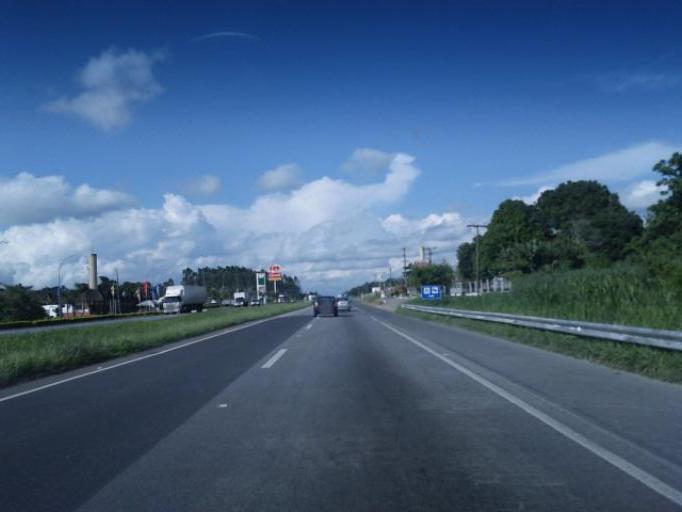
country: BR
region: Sao Paulo
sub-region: Registro
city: Registro
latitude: -24.4783
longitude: -47.8289
